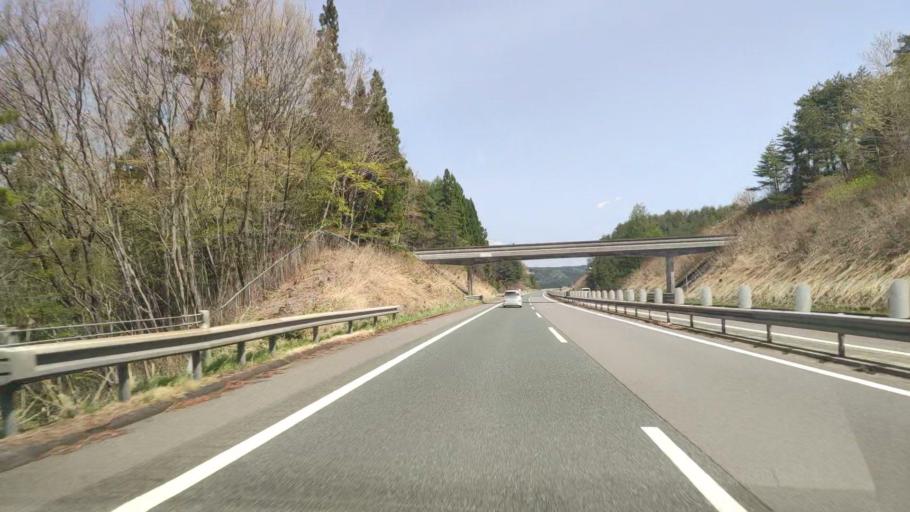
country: JP
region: Iwate
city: Ichinohe
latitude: 40.1516
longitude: 141.1184
